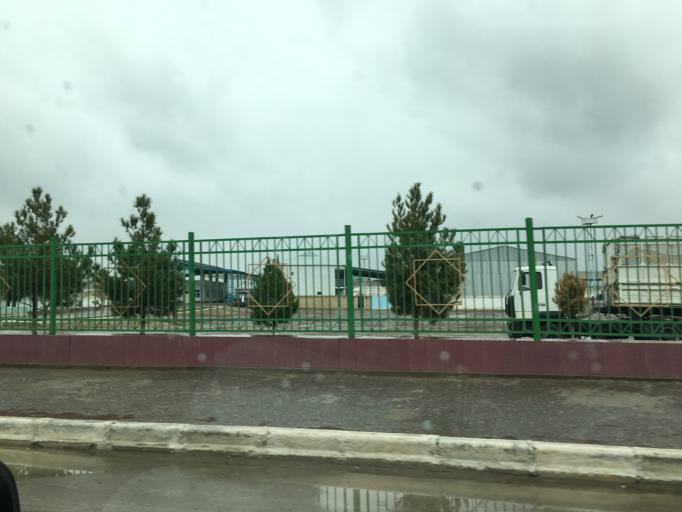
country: TM
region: Mary
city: Yoloeten
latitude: 37.2908
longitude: 62.3580
